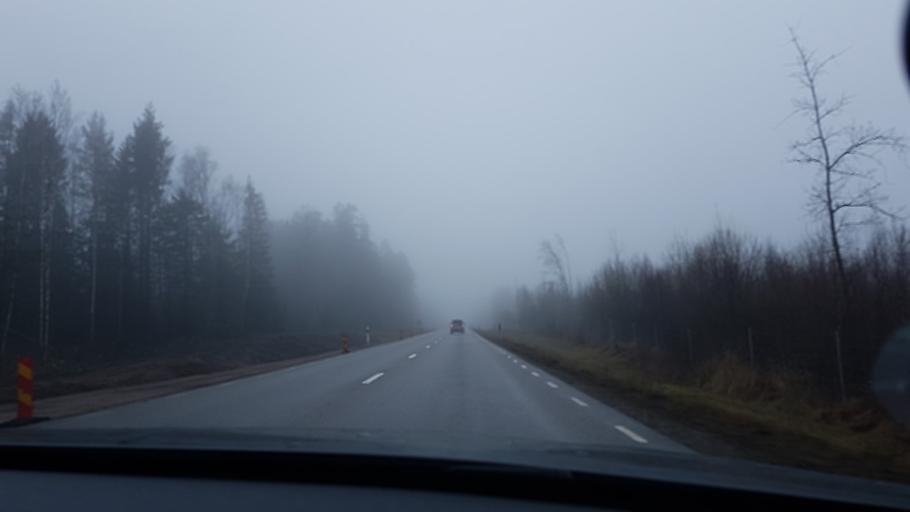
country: SE
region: Vaestra Goetaland
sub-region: Gullspangs Kommun
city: Gullspang
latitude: 58.9592
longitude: 14.0586
